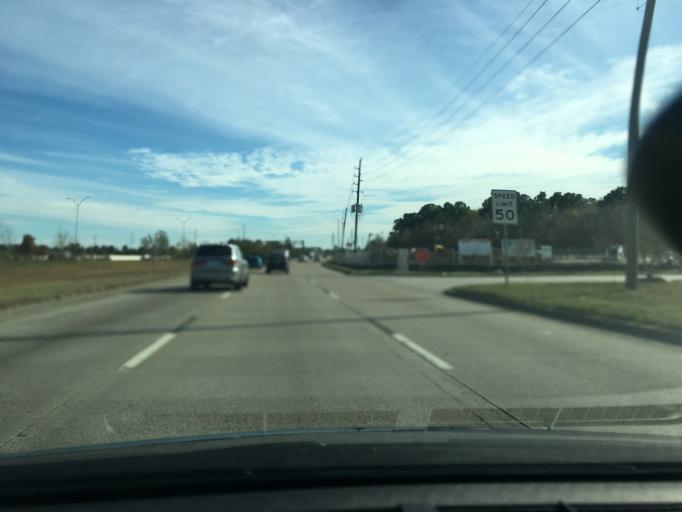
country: US
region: Texas
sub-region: Harris County
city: Cloverleaf
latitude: 29.8250
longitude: -95.1699
